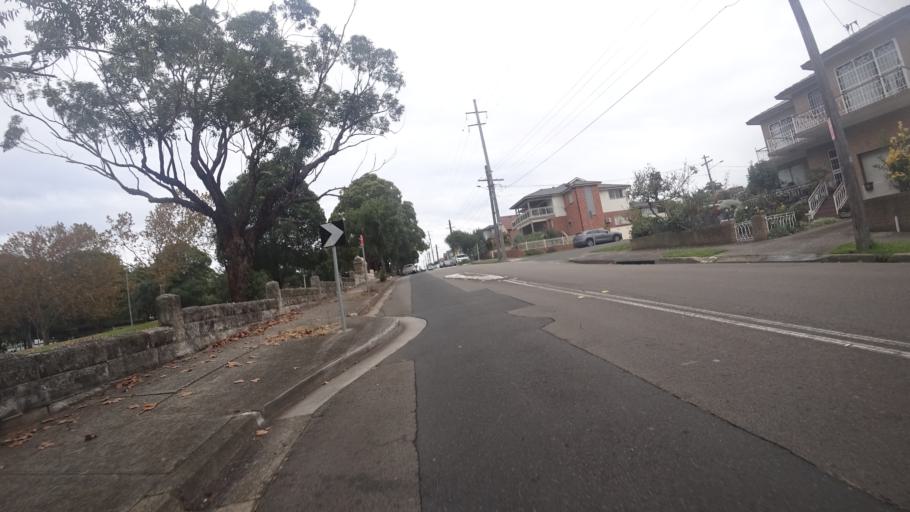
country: AU
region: New South Wales
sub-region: Rockdale
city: Bardwell Valley
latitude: -33.9342
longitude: 151.1422
